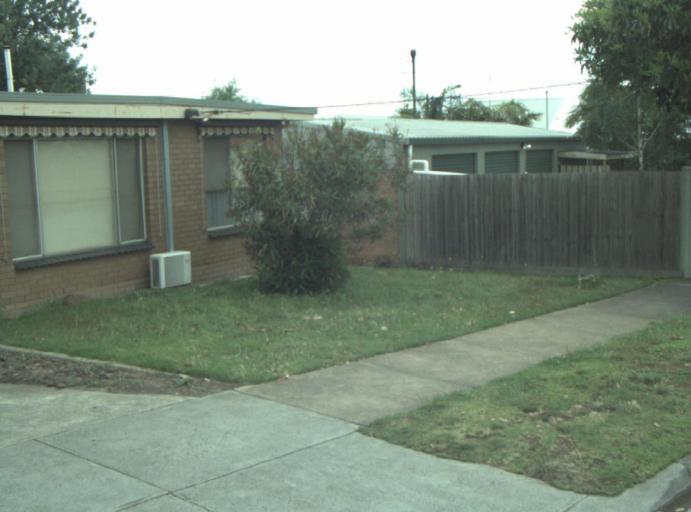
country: AU
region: Victoria
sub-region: Greater Geelong
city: Breakwater
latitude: -38.1817
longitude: 144.3668
